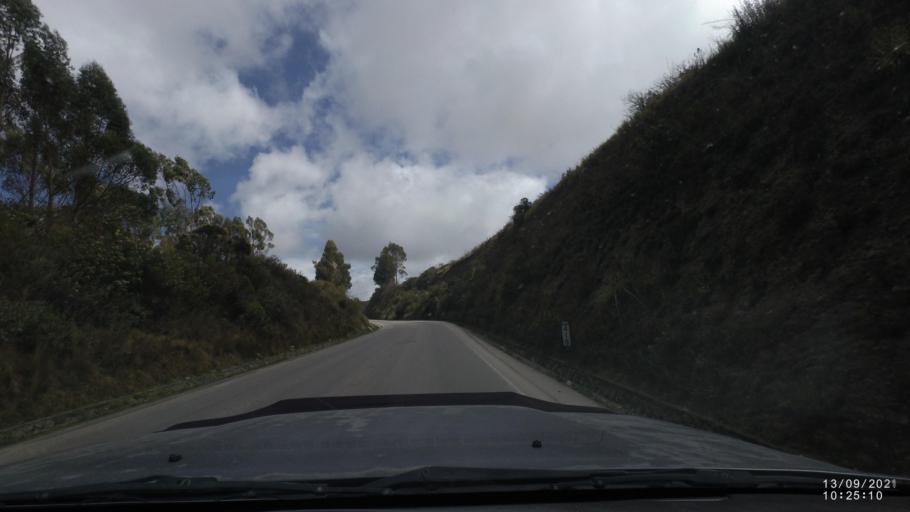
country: BO
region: Cochabamba
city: Colomi
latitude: -17.3135
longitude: -65.8628
